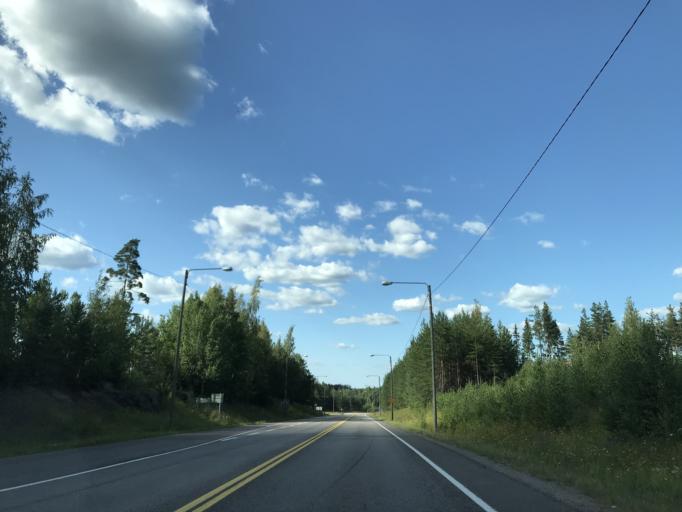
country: FI
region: Uusimaa
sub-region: Helsinki
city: Nurmijaervi
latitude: 60.4530
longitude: 24.8332
